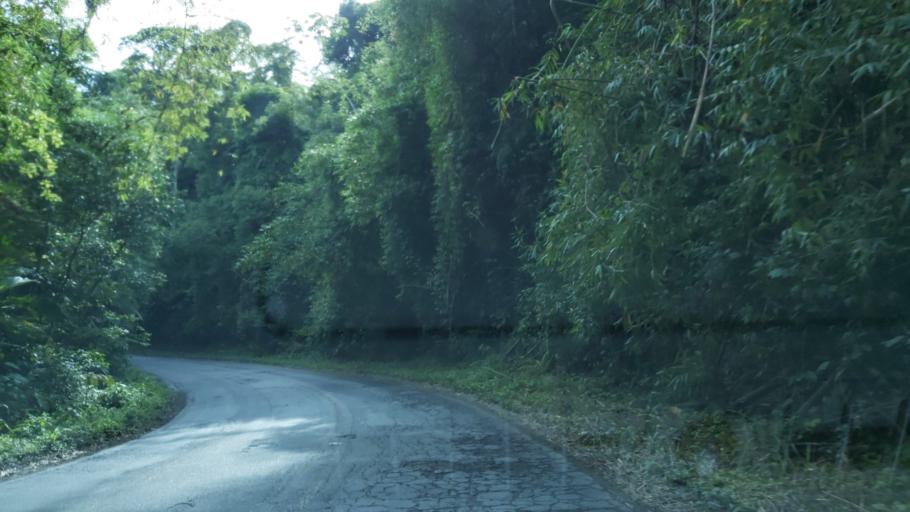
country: BR
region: Sao Paulo
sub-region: Miracatu
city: Miracatu
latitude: -24.0544
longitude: -47.5785
